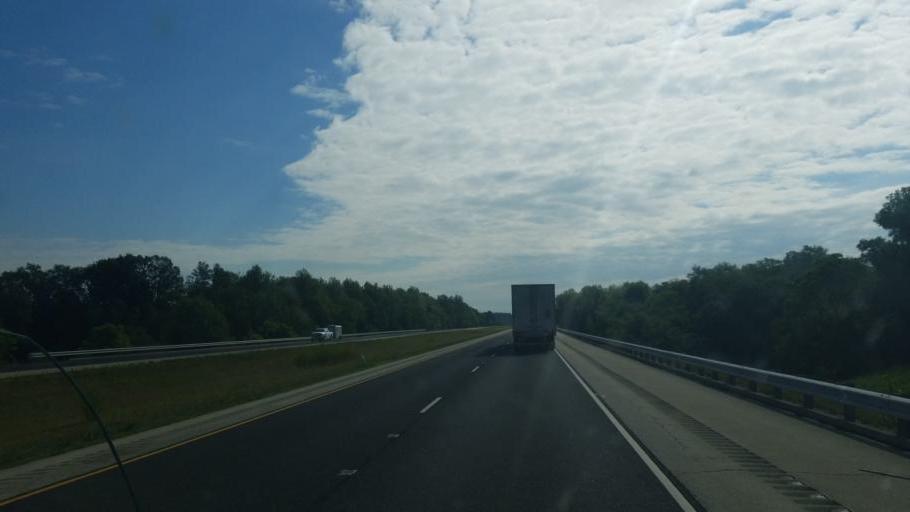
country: US
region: Illinois
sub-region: Clark County
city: Martinsville
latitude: 39.3901
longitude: -87.8052
